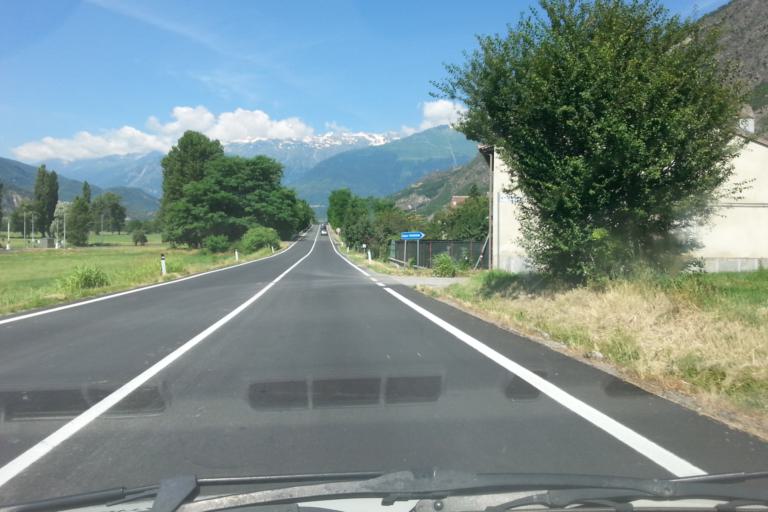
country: IT
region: Piedmont
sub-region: Provincia di Torino
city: Mattie
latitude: 45.1367
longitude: 7.1108
